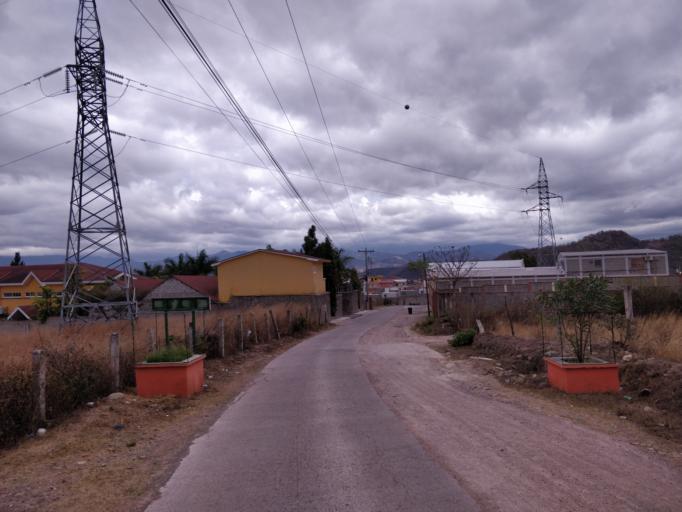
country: HN
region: Francisco Morazan
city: Yaguacire
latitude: 14.0345
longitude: -87.2435
